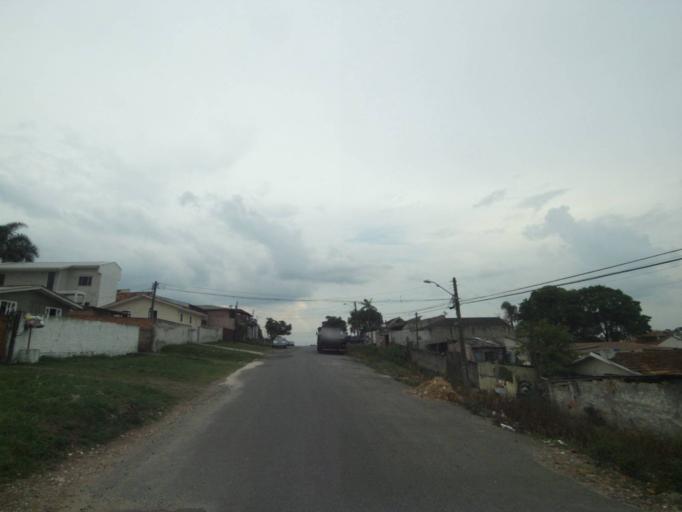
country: BR
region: Parana
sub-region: Pinhais
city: Pinhais
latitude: -25.4070
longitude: -49.1998
